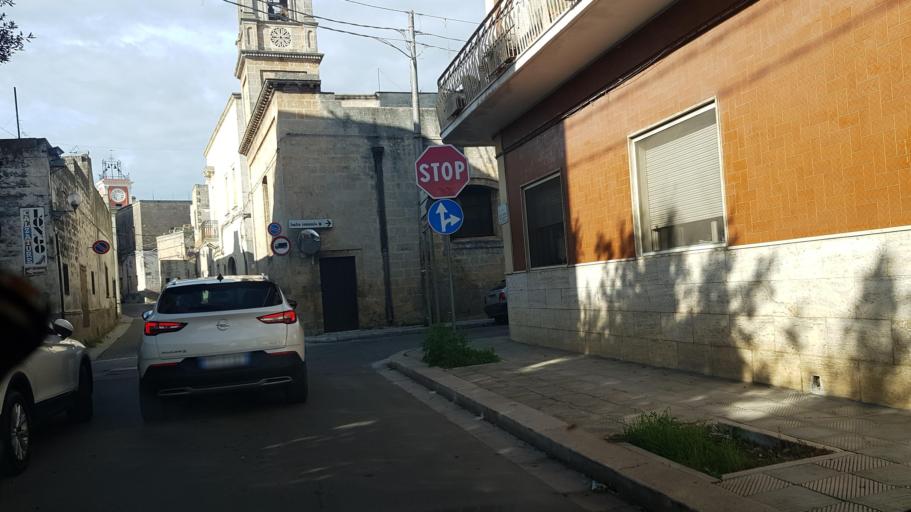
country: IT
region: Apulia
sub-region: Provincia di Brindisi
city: Torre Santa Susanna
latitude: 40.4644
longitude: 17.7416
